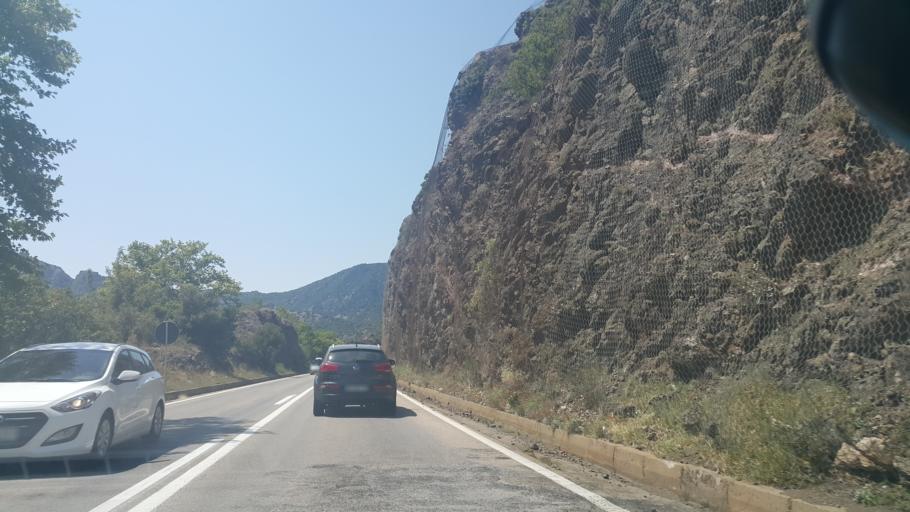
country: MK
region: Demir Kapija
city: Demir Kapija
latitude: 41.4076
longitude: 22.2860
